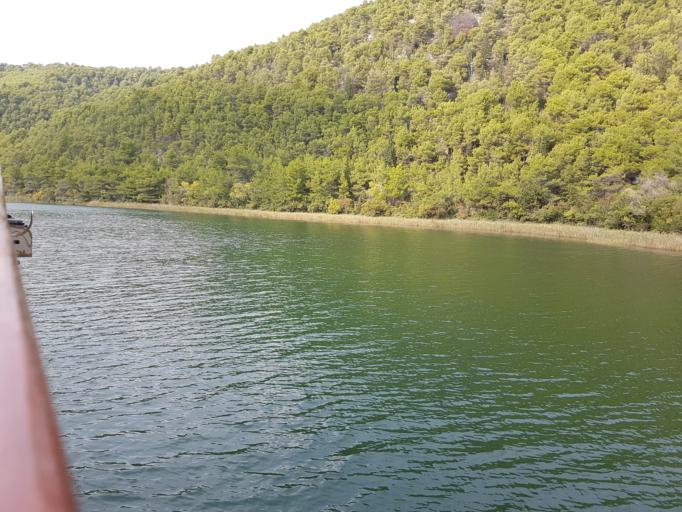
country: HR
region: Sibensko-Kniniska
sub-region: Grad Sibenik
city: Sibenik
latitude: 43.8198
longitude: 15.9477
